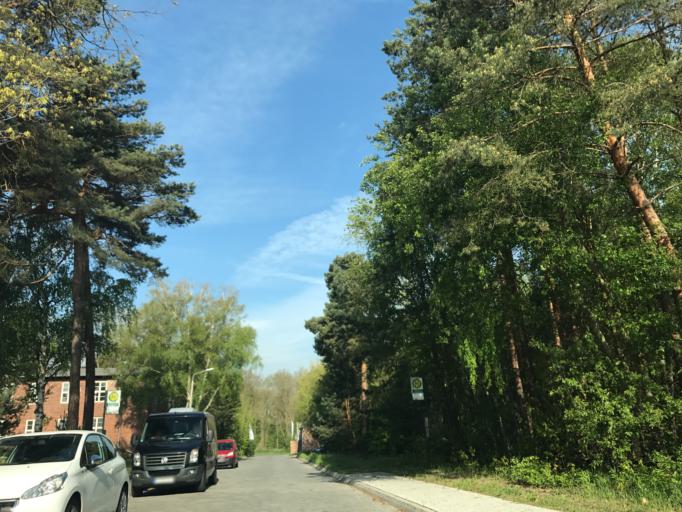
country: DE
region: Berlin
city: Kladow
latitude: 52.4863
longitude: 13.1252
